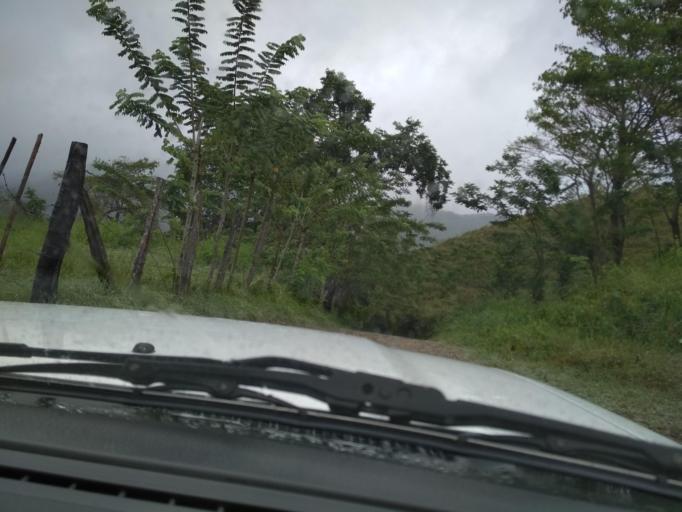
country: MX
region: Veracruz
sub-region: Chalma
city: San Pedro Coyutla
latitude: 21.2302
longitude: -98.4504
